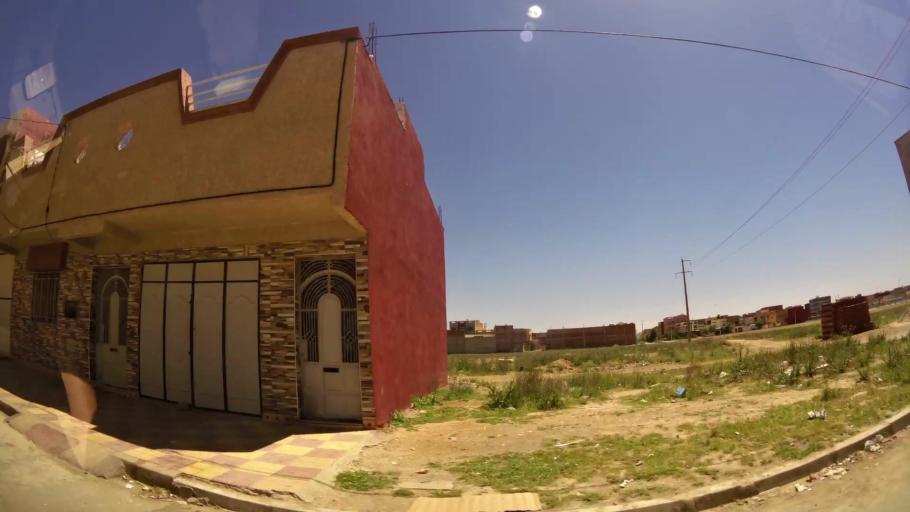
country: MA
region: Oriental
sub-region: Oujda-Angad
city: Oujda
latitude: 34.6799
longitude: -1.8574
